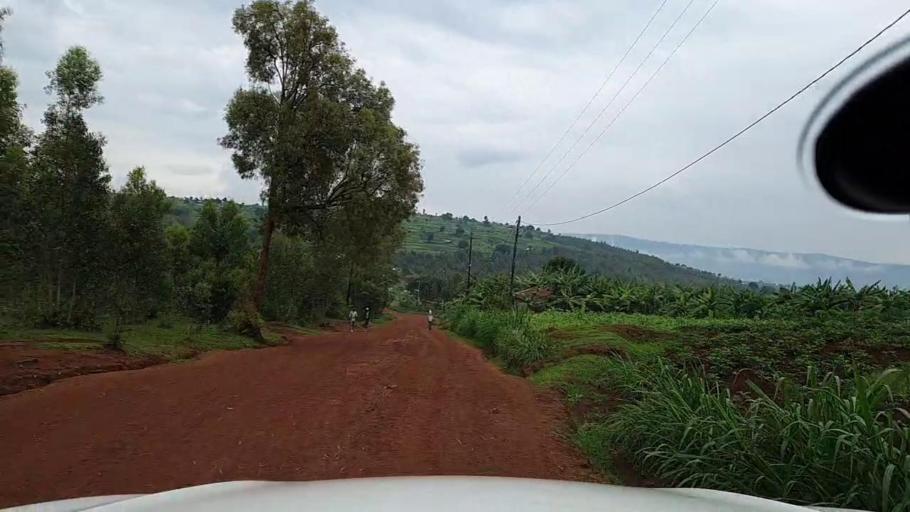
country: RW
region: Kigali
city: Kigali
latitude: -1.9082
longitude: 29.8983
